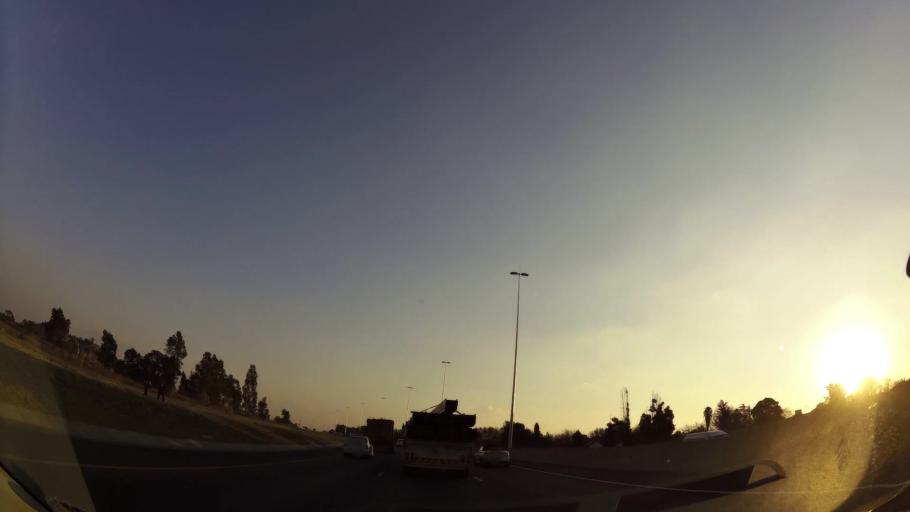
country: ZA
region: Gauteng
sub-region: Ekurhuleni Metropolitan Municipality
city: Benoni
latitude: -26.1637
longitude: 28.3596
